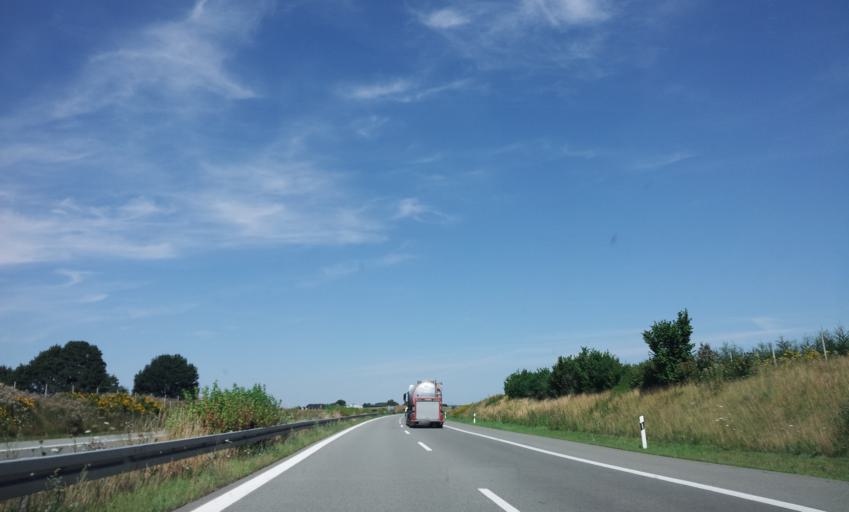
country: DE
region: Mecklenburg-Vorpommern
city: Neuenkirchen
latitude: 53.6245
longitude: 13.3669
